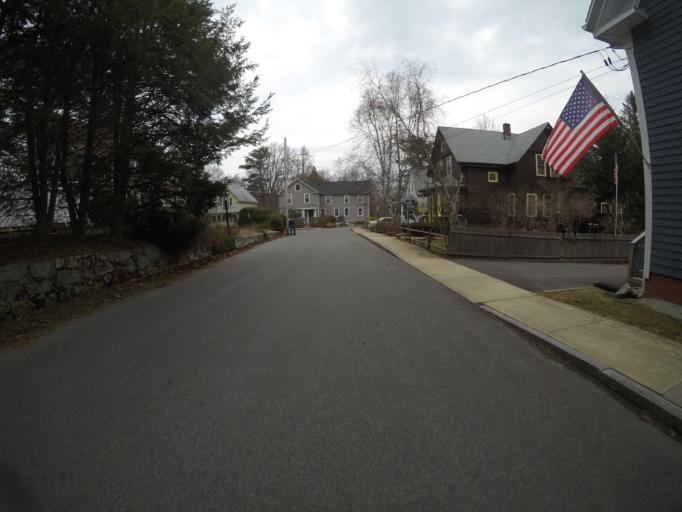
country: US
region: Massachusetts
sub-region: Norfolk County
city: Stoughton
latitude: 42.0724
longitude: -71.1041
